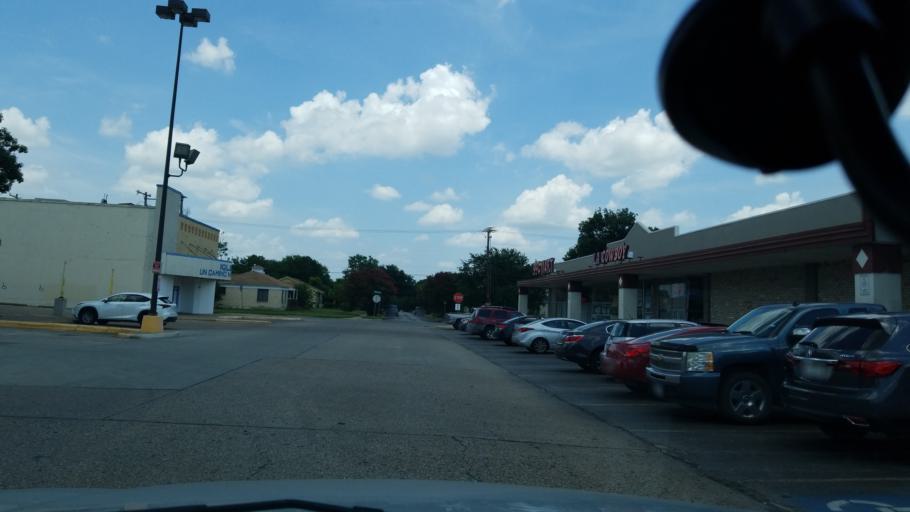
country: US
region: Texas
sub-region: Dallas County
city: Cockrell Hill
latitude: 32.7264
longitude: -96.8729
